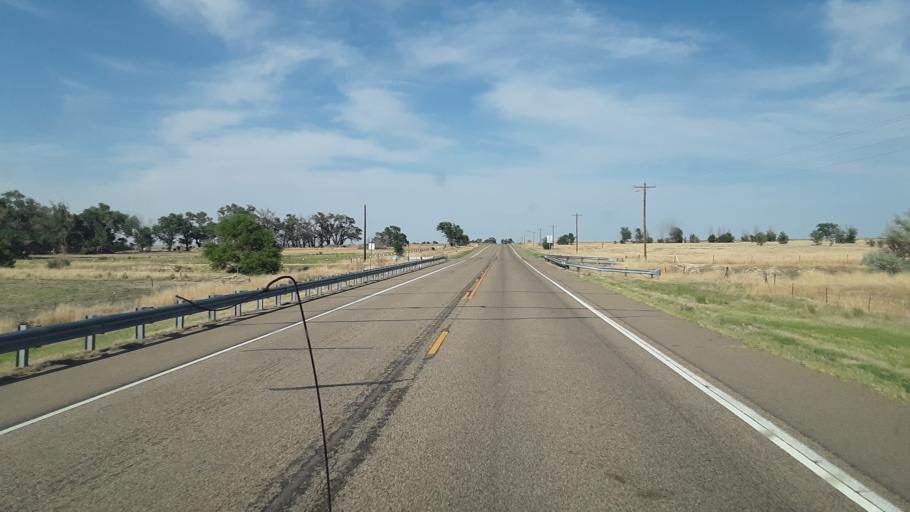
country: US
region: Colorado
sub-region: Bent County
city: Las Animas
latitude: 38.1094
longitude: -103.1073
